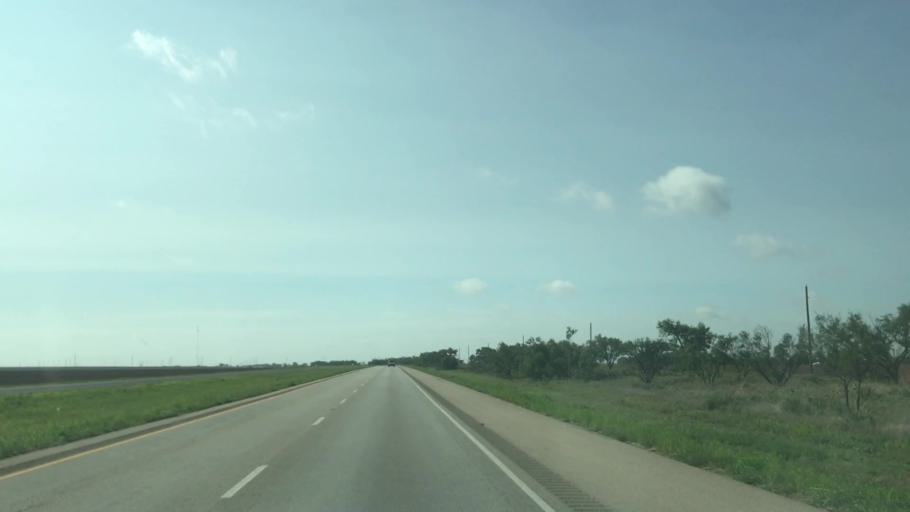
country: US
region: Texas
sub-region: Nolan County
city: Roscoe
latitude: 32.5793
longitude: -100.7240
